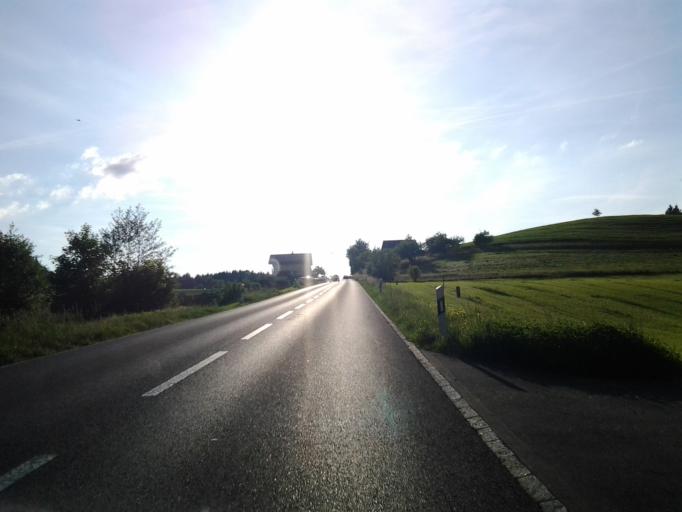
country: CH
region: Aargau
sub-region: Bezirk Zofingen
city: Brittnau
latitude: 47.2455
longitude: 7.9507
